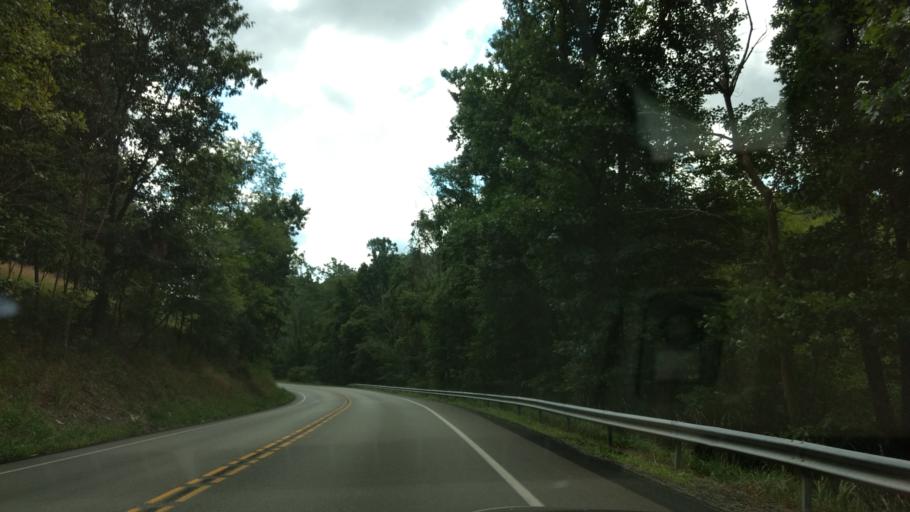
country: US
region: Pennsylvania
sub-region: Armstrong County
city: Apollo
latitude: 40.5353
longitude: -79.6392
